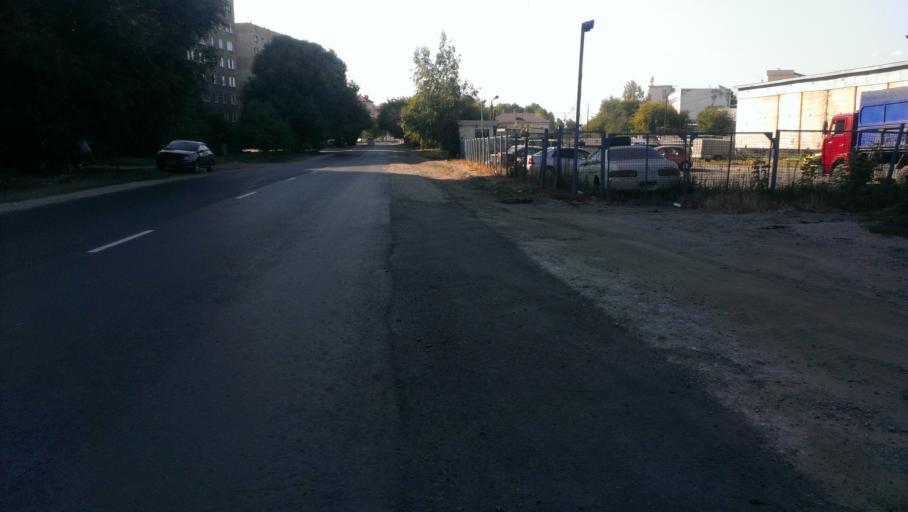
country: RU
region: Altai Krai
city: Novosilikatnyy
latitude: 53.3061
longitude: 83.6252
